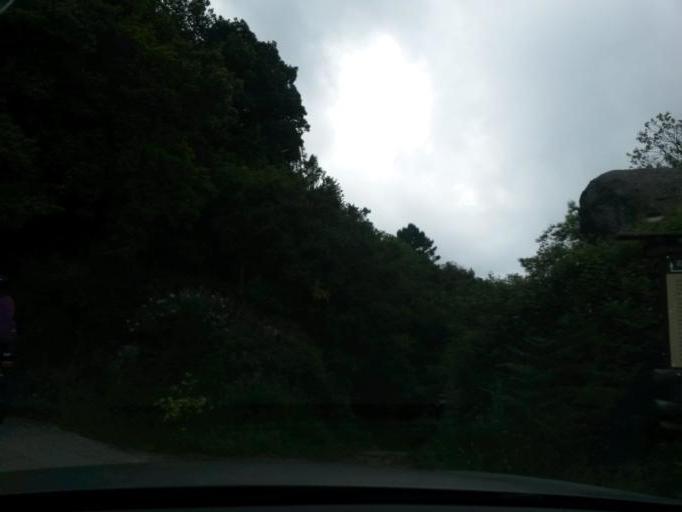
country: IT
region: Tuscany
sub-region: Provincia di Livorno
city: Campo nell'Elba
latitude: 42.7636
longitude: 10.1980
